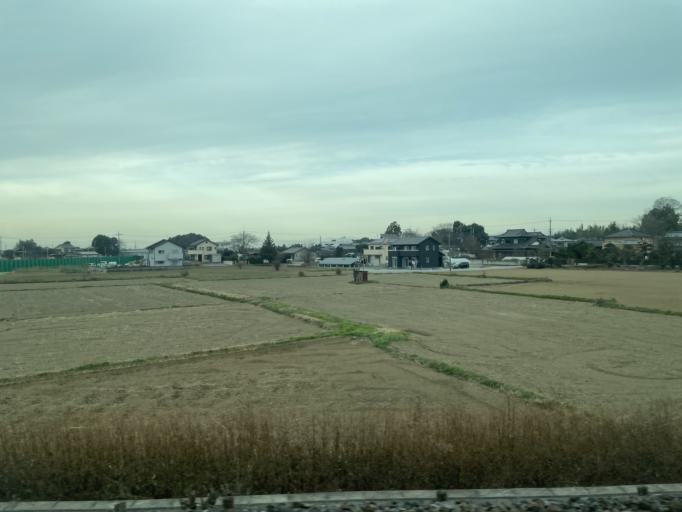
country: JP
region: Saitama
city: Kurihashi
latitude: 36.1543
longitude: 139.7109
